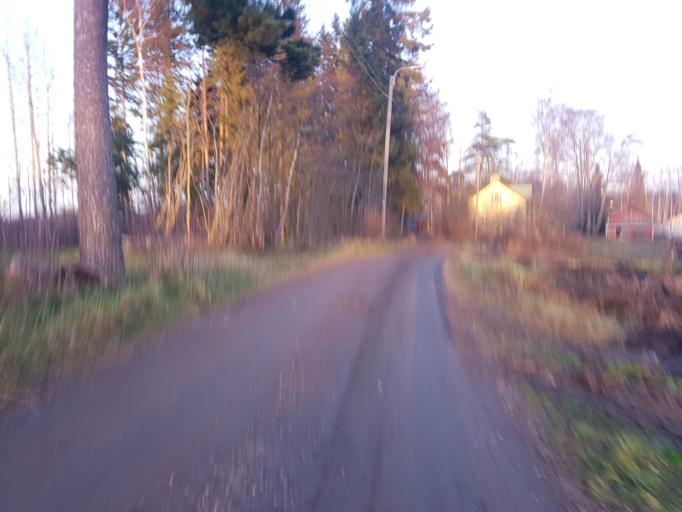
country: FI
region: Uusimaa
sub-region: Helsinki
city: Helsinki
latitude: 60.2762
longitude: 24.9193
